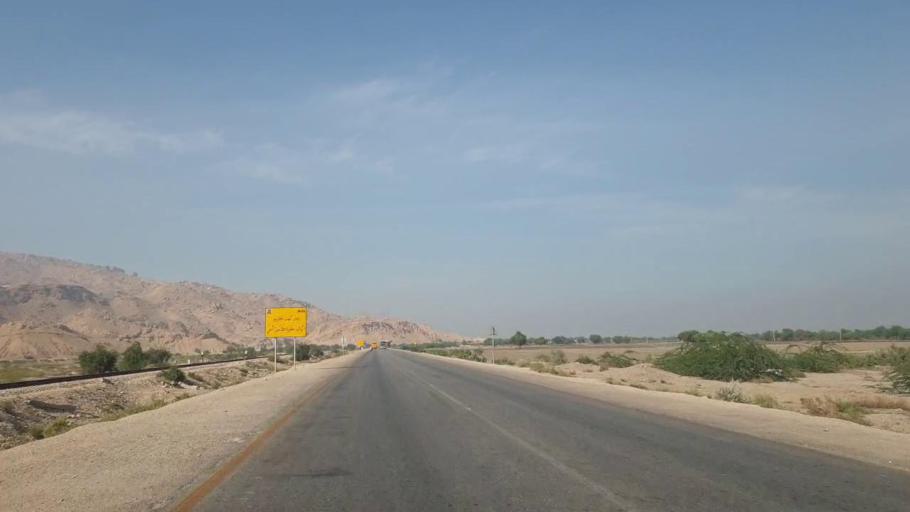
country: PK
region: Sindh
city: Sehwan
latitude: 26.2819
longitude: 67.8959
